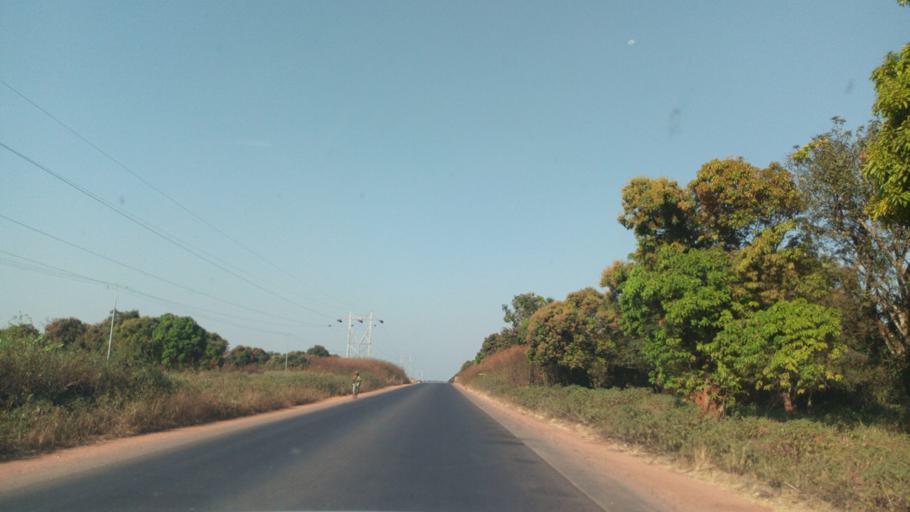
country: CD
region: Katanga
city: Likasi
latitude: -11.0012
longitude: 26.8744
